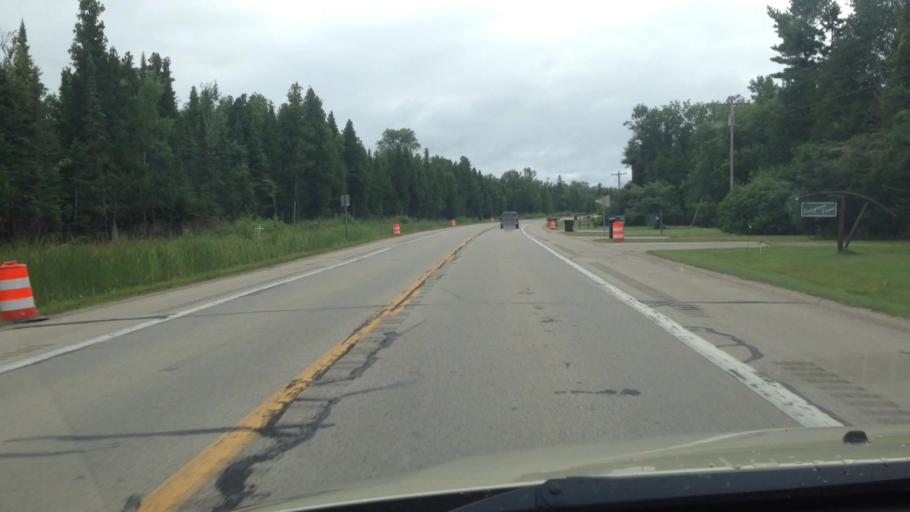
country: US
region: Michigan
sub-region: Delta County
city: Escanaba
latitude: 45.6463
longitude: -87.1873
